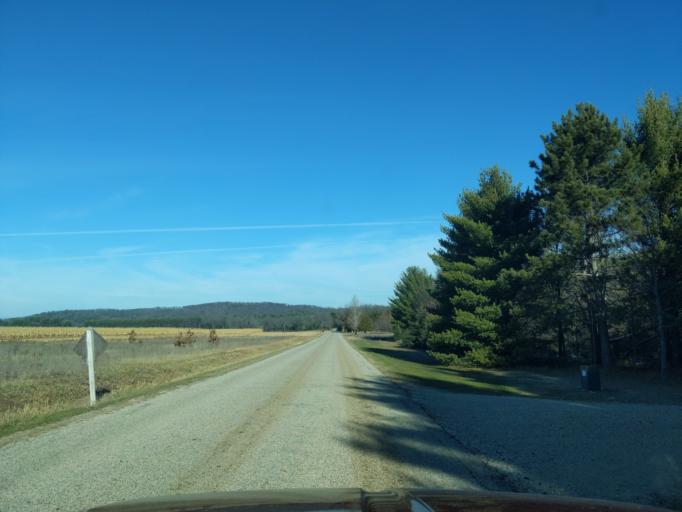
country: US
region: Wisconsin
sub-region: Waushara County
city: Silver Lake
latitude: 44.0986
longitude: -89.1788
